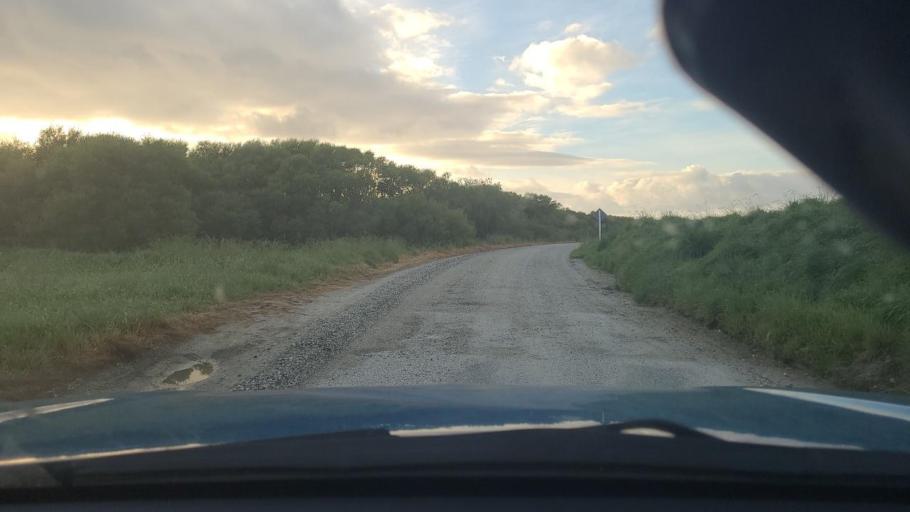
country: NZ
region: Southland
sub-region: Invercargill City
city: Invercargill
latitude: -46.5108
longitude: 168.7365
